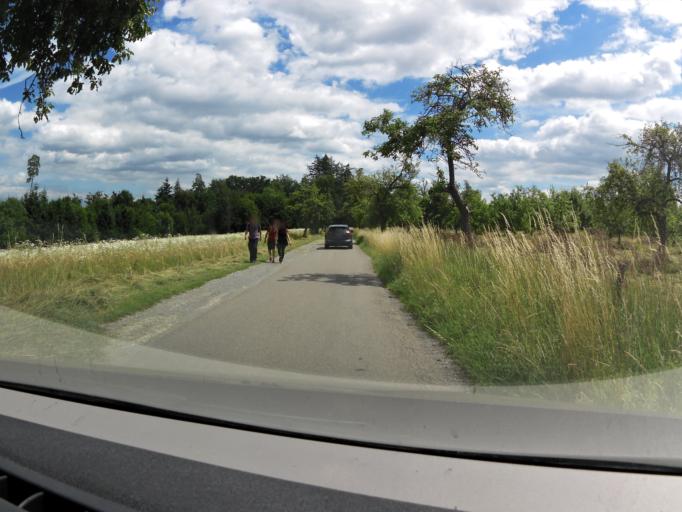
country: DE
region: Baden-Wuerttemberg
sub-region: Tuebingen Region
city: Tuebingen
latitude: 48.5531
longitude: 8.9915
